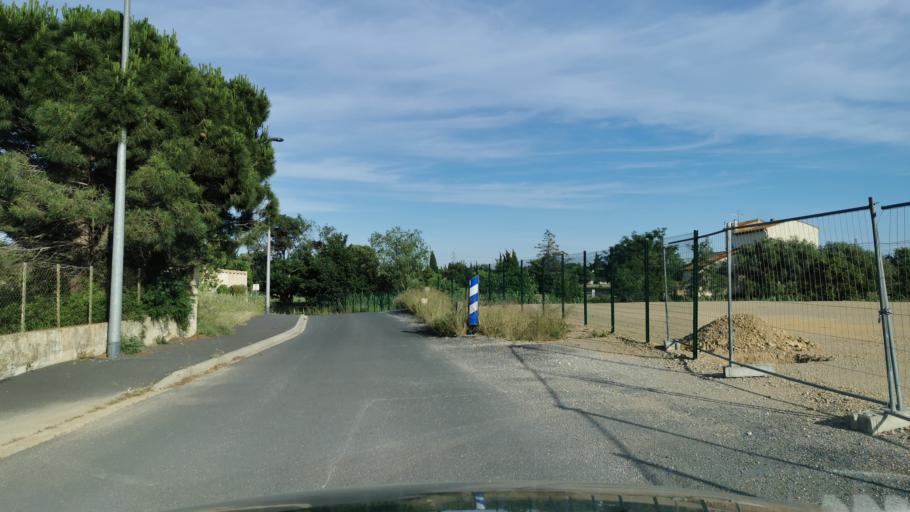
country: FR
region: Languedoc-Roussillon
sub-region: Departement de l'Aude
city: Narbonne
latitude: 43.1696
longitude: 2.9934
